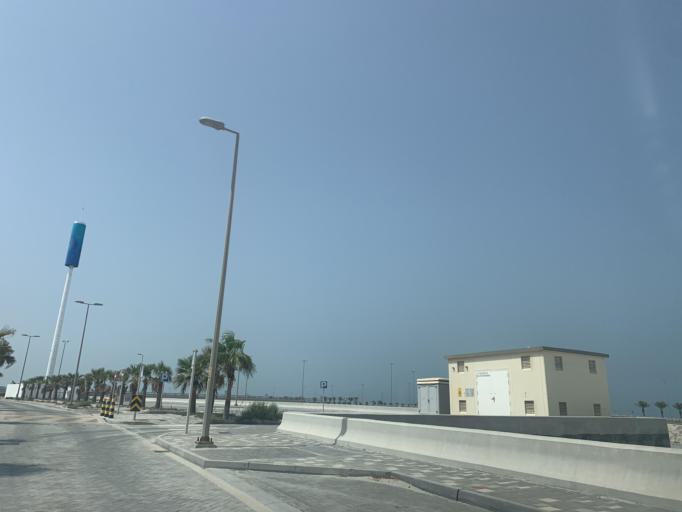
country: BH
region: Muharraq
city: Al Hadd
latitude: 26.2732
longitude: 50.6758
